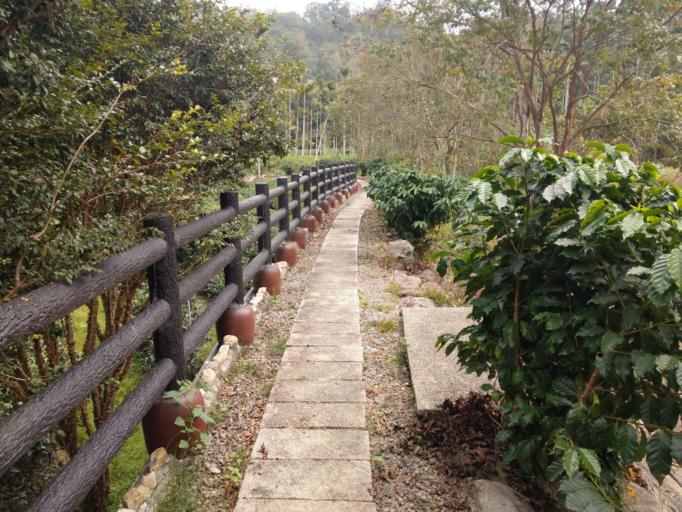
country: TW
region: Taiwan
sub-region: Nantou
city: Puli
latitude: 23.9190
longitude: 120.9205
